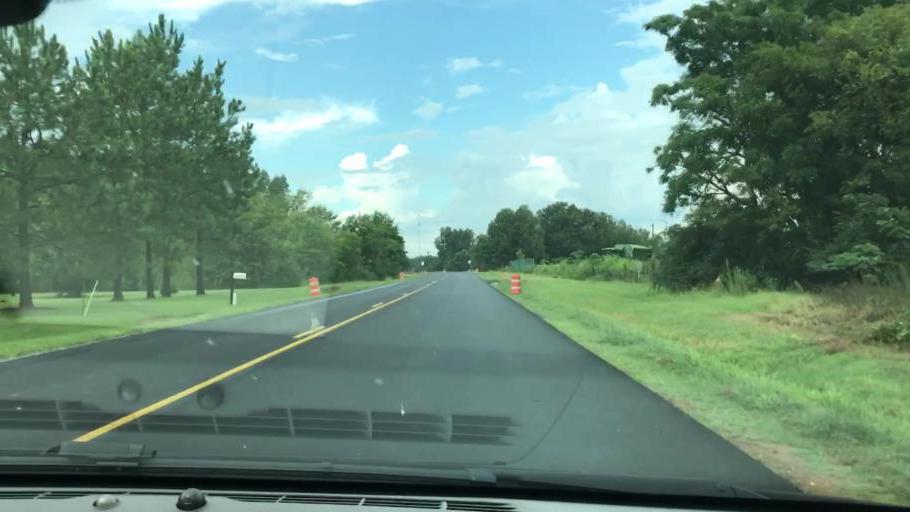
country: US
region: Georgia
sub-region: Early County
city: Blakely
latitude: 31.3937
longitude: -84.9482
